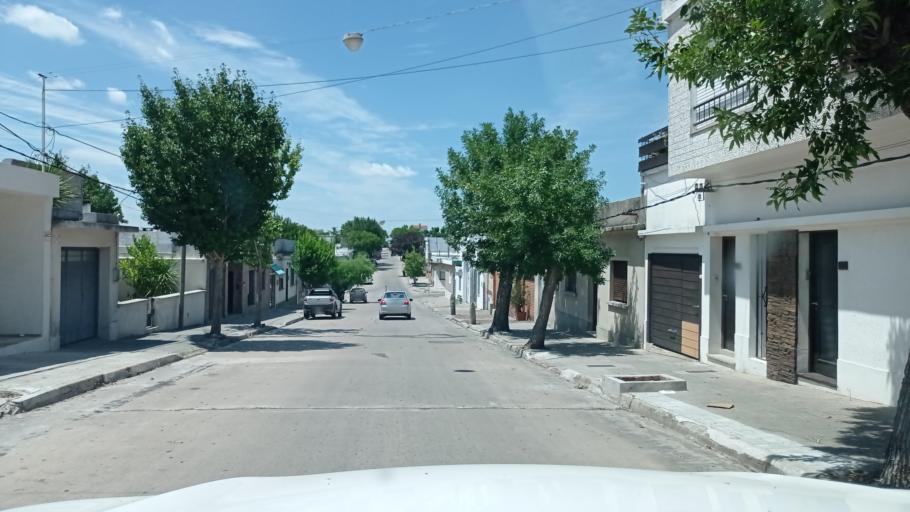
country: UY
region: Florida
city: Florida
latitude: -34.0934
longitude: -56.2154
